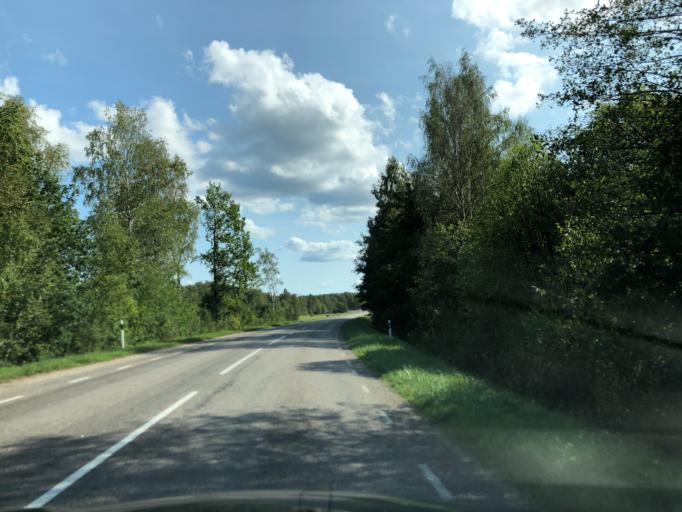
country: EE
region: Hiiumaa
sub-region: Kaerdla linn
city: Kardla
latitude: 58.7238
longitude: 22.5616
